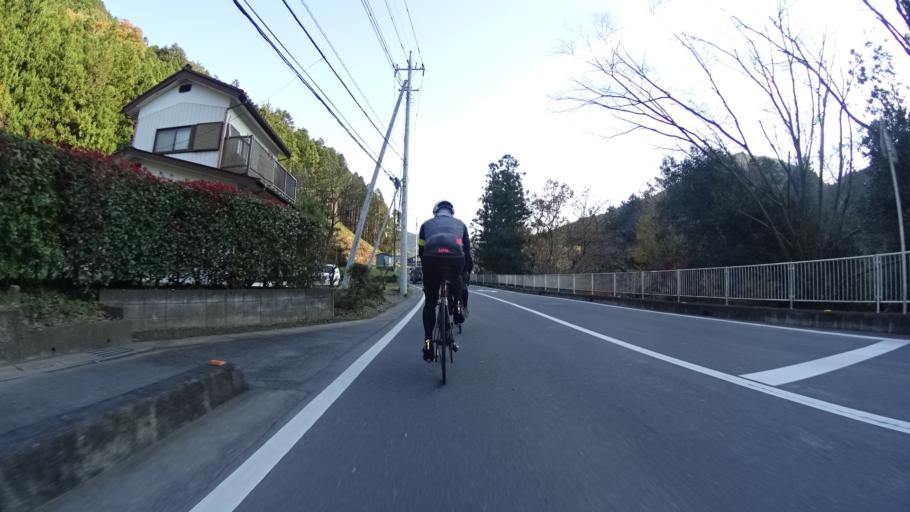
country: JP
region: Saitama
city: Hanno
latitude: 35.8702
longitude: 139.2657
